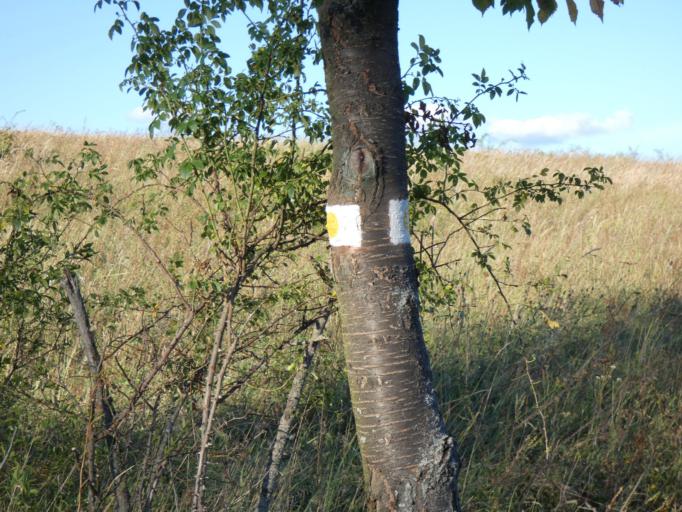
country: HU
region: Pest
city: Telki
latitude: 47.5792
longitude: 18.8584
